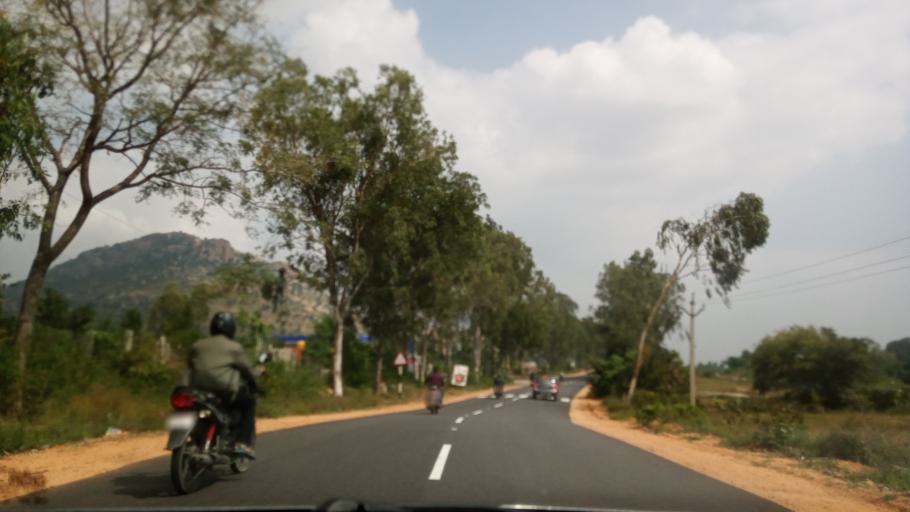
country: IN
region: Andhra Pradesh
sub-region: Chittoor
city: Madanapalle
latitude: 13.6360
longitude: 78.5996
